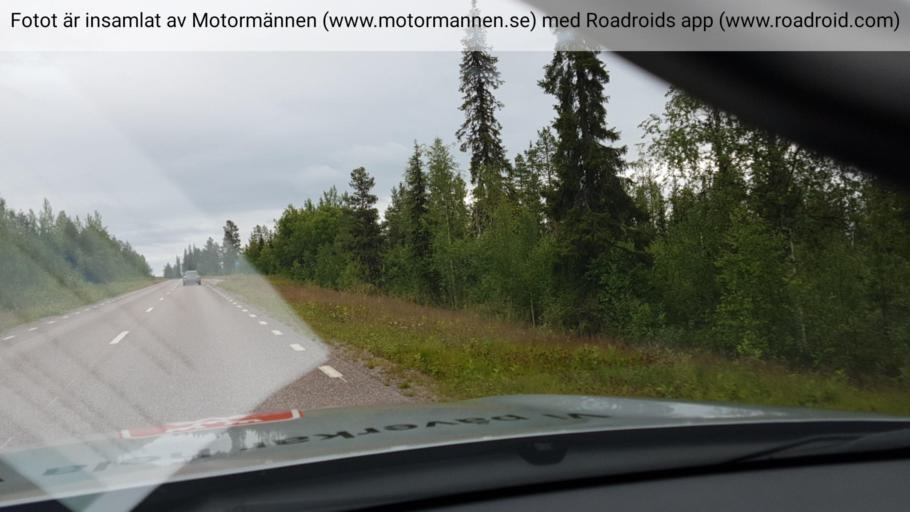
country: SE
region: Norrbotten
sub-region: Gallivare Kommun
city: Gaellivare
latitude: 67.0489
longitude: 21.6103
